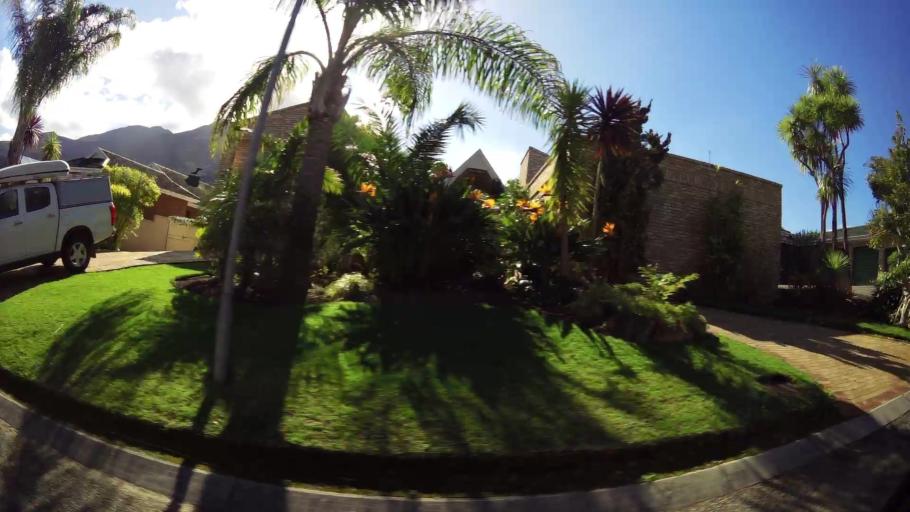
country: ZA
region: Western Cape
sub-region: Eden District Municipality
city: George
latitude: -33.9472
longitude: 22.4619
